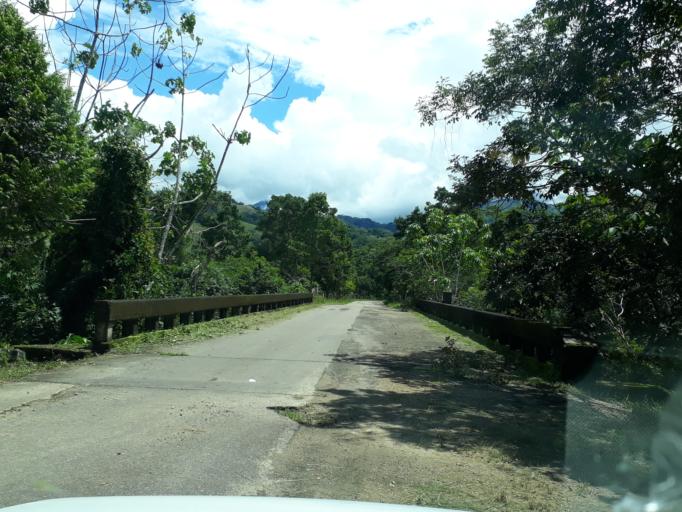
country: CO
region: Cundinamarca
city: Medina
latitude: 4.5767
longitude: -73.3266
